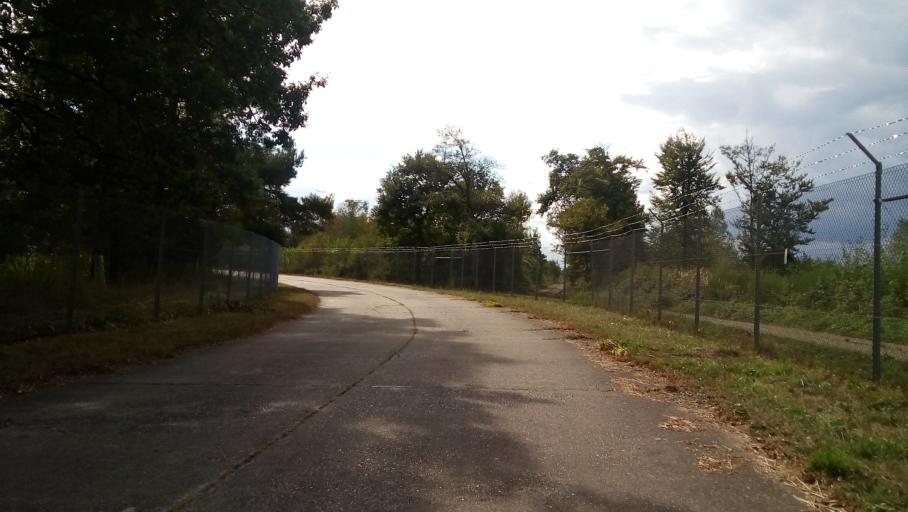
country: DE
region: Baden-Wuerttemberg
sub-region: Karlsruhe Region
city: Schwarzach
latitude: 48.7657
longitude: 8.0764
